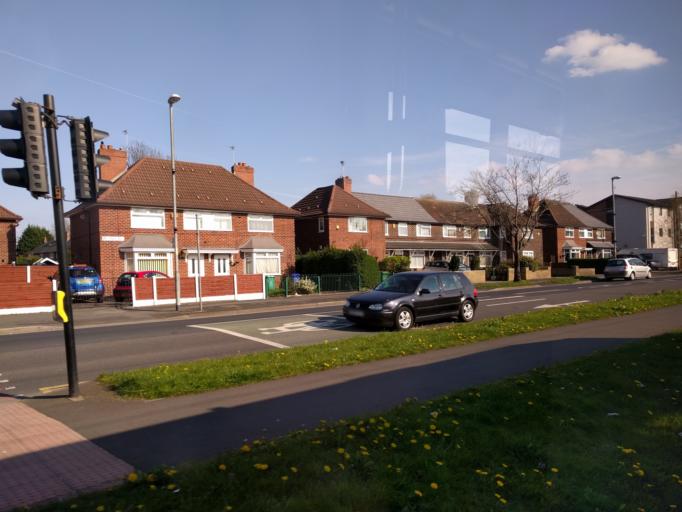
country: GB
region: England
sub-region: Manchester
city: Didsbury
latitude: 53.3856
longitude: -2.2560
